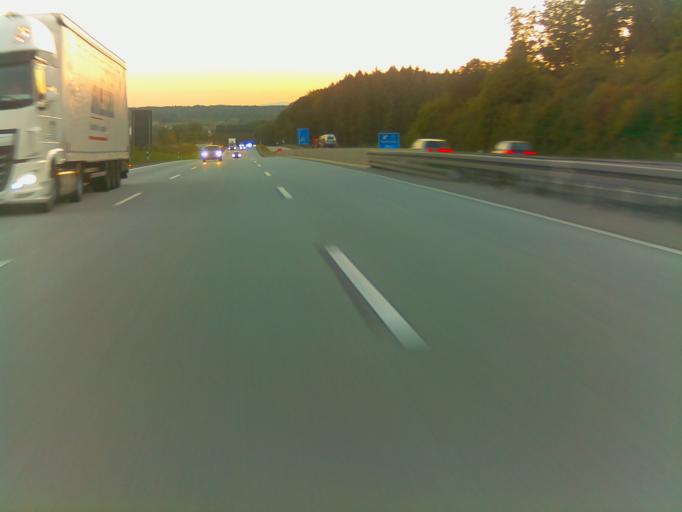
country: DE
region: Hesse
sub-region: Regierungsbezirk Giessen
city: Reiskirchen
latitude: 50.6063
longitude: 8.8219
